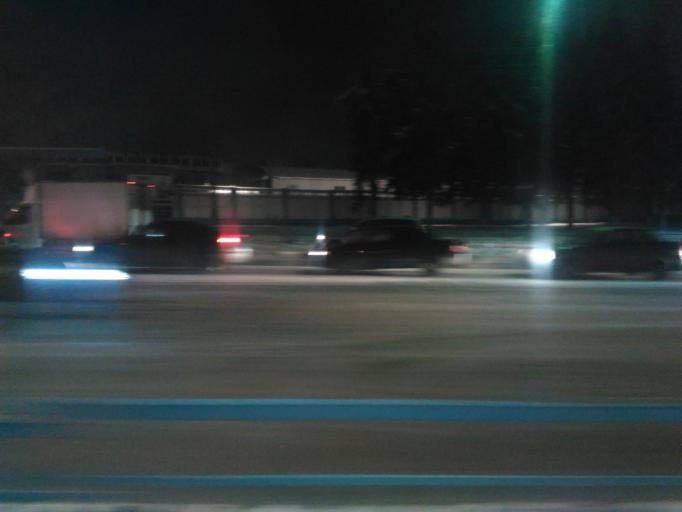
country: RU
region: Ulyanovsk
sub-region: Ulyanovskiy Rayon
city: Ulyanovsk
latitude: 54.3160
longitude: 48.3566
